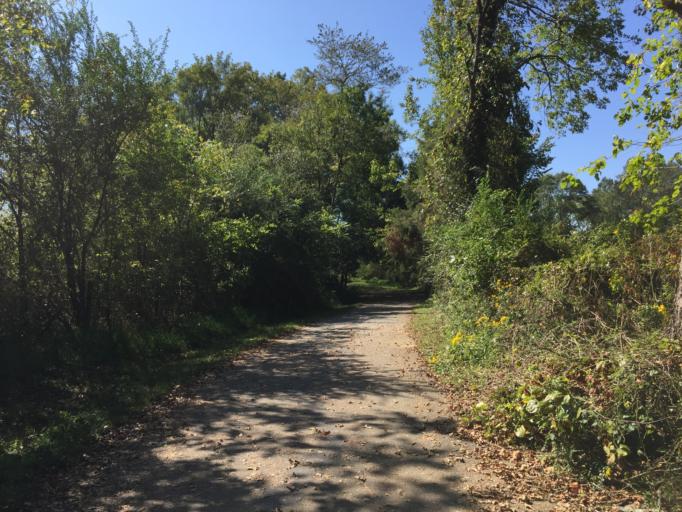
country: US
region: Georgia
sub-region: Gwinnett County
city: Duluth
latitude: 34.0313
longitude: -84.1412
